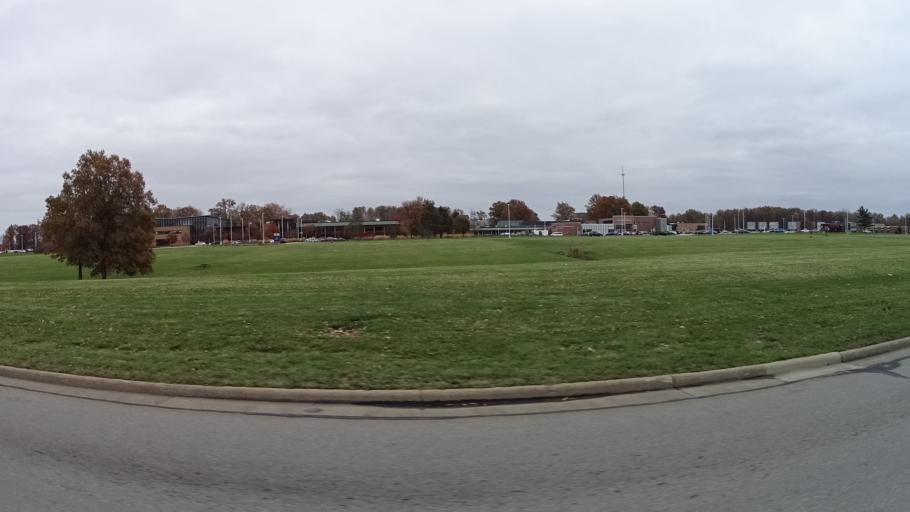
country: US
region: Ohio
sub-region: Lorain County
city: Sheffield
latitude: 41.4127
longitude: -82.0770
